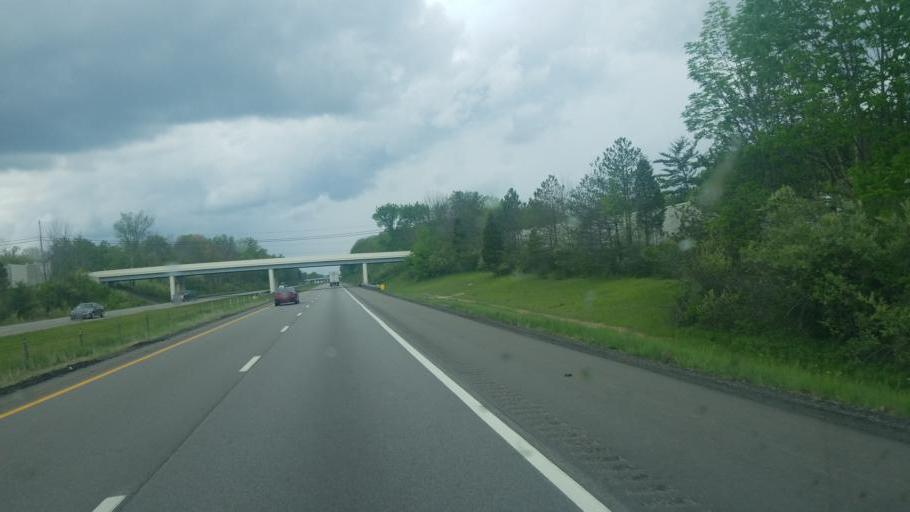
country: US
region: Ohio
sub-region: Mahoning County
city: Craig Beach
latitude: 41.1004
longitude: -80.9873
